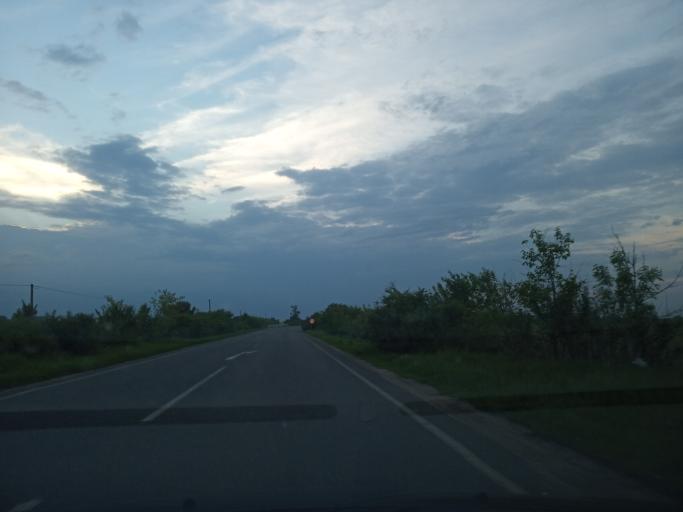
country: RO
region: Timis
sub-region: Comuna Denta
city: Denta
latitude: 45.3710
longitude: 21.2380
